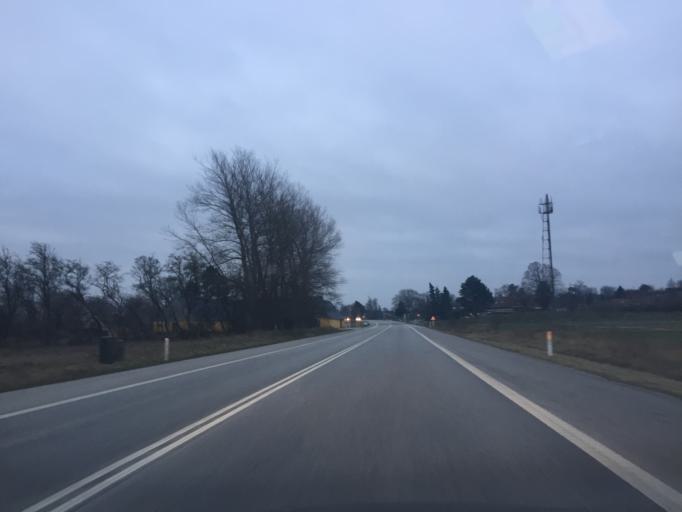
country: DK
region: Capital Region
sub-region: Halsnaes Kommune
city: Frederiksvaerk
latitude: 55.9369
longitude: 12.0479
